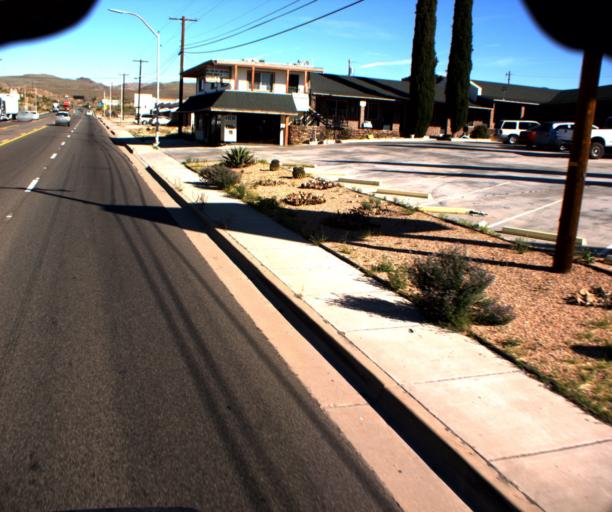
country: US
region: Arizona
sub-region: Mohave County
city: Kingman
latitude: 35.1960
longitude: -114.0748
